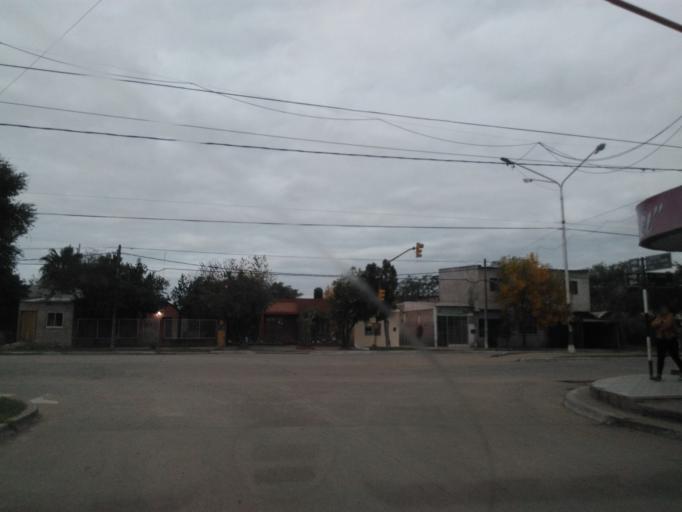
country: AR
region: Chaco
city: Resistencia
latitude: -27.4728
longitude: -58.9911
